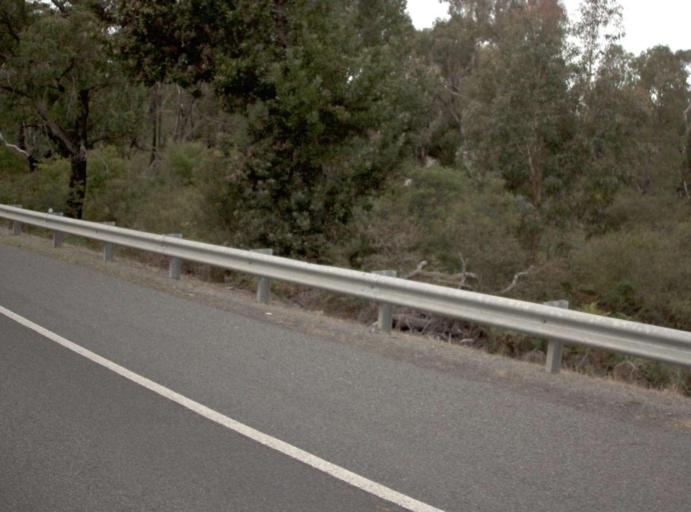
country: AU
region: Victoria
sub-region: Wellington
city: Sale
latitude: -38.3322
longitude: 147.0173
